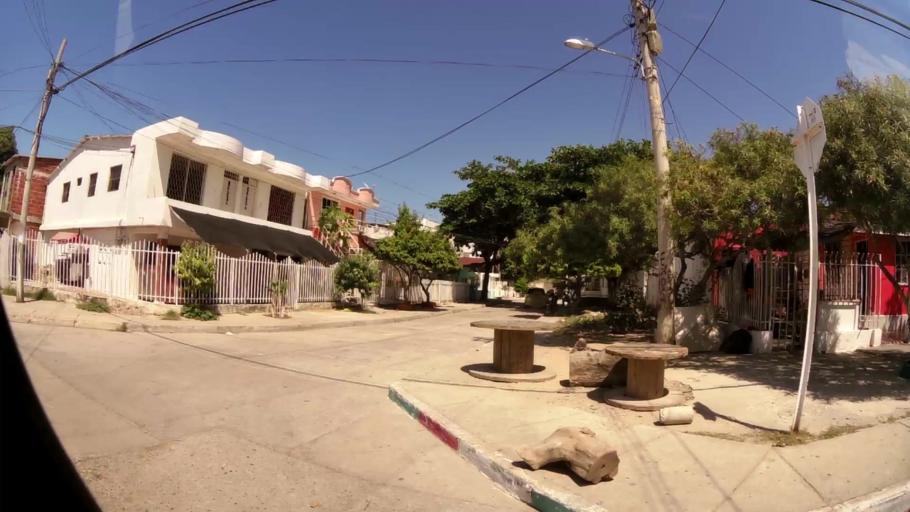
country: CO
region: Bolivar
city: Cartagena
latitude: 10.4342
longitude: -75.5282
